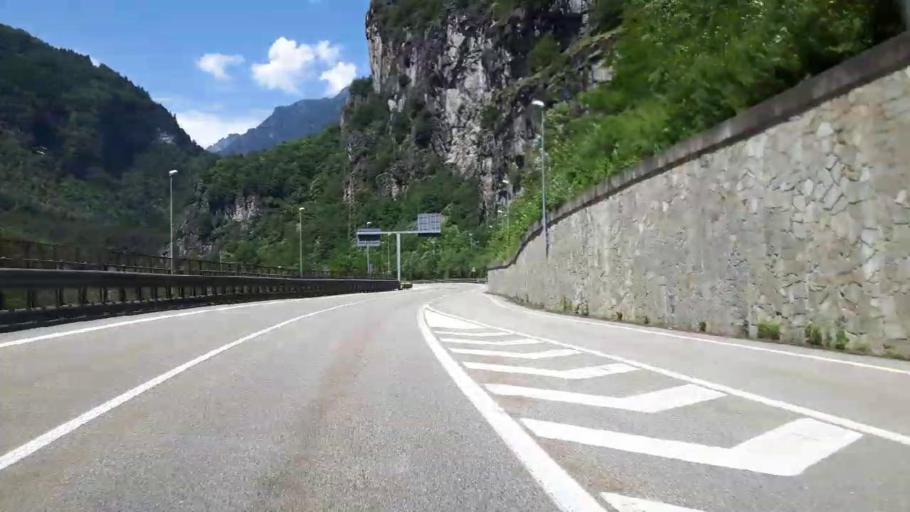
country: IT
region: Piedmont
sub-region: Provincia Verbano-Cusio-Ossola
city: Trasquera
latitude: 46.2060
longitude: 8.2227
